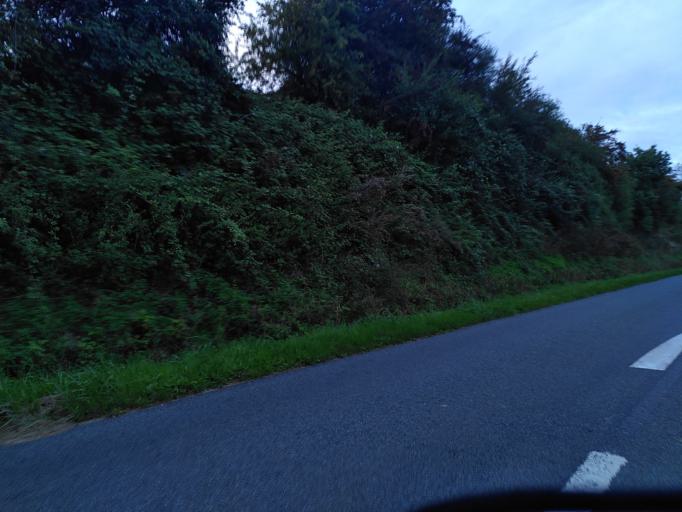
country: FR
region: Nord-Pas-de-Calais
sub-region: Departement du Pas-de-Calais
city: Therouanne
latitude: 50.6438
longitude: 2.2655
